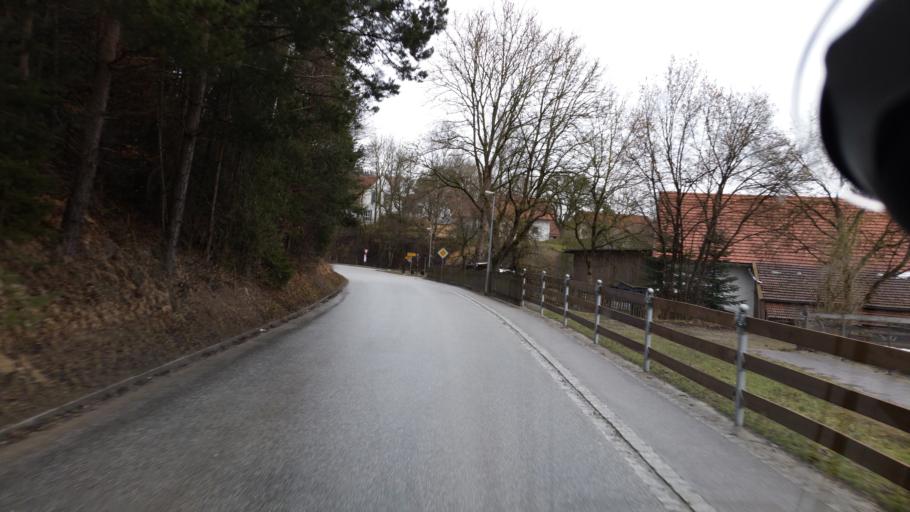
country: DE
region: Bavaria
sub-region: Lower Bavaria
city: Eching
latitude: 48.4963
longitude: 12.0651
